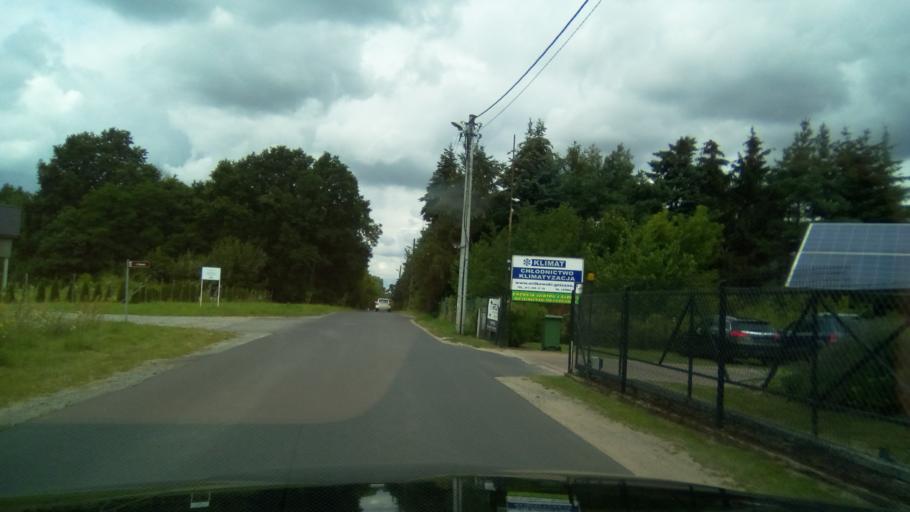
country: PL
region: Greater Poland Voivodeship
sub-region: Powiat gnieznienski
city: Gniezno
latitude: 52.5174
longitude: 17.6211
